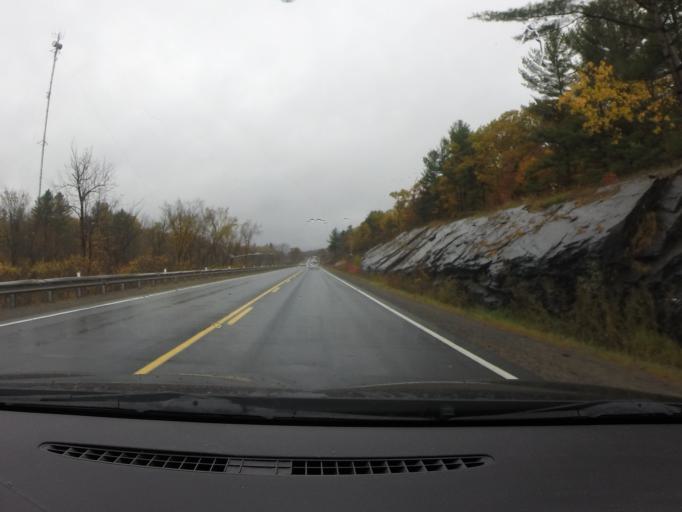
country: CA
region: Ontario
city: Greater Napanee
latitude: 44.6379
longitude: -77.1348
